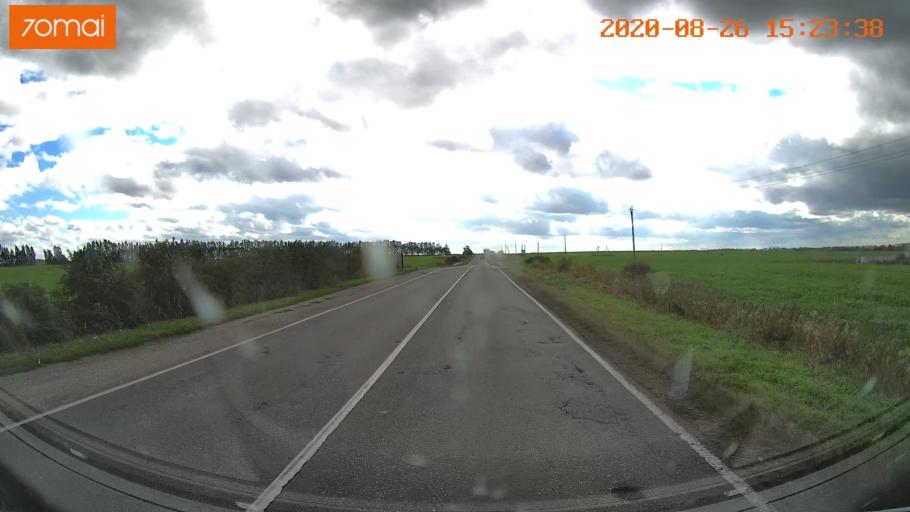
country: RU
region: Tula
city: Severo-Zadonsk
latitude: 54.1214
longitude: 38.4541
